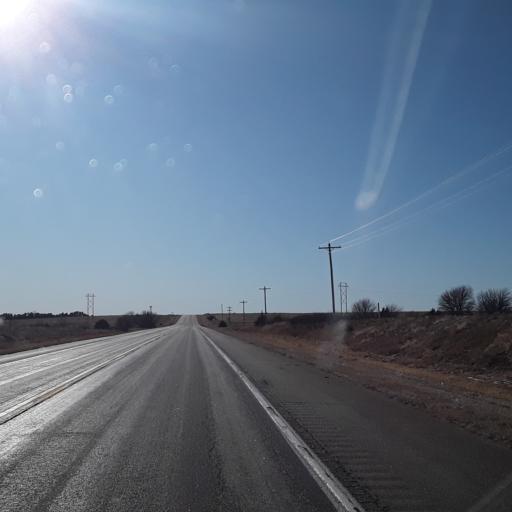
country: US
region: Nebraska
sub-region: Frontier County
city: Stockville
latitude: 40.5534
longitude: -100.6372
